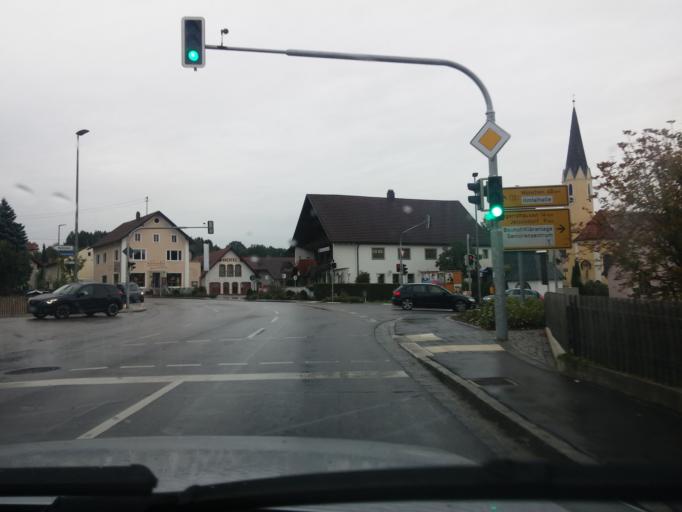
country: DE
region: Bavaria
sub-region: Upper Bavaria
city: Reichertshausen
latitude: 48.4665
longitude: 11.5077
